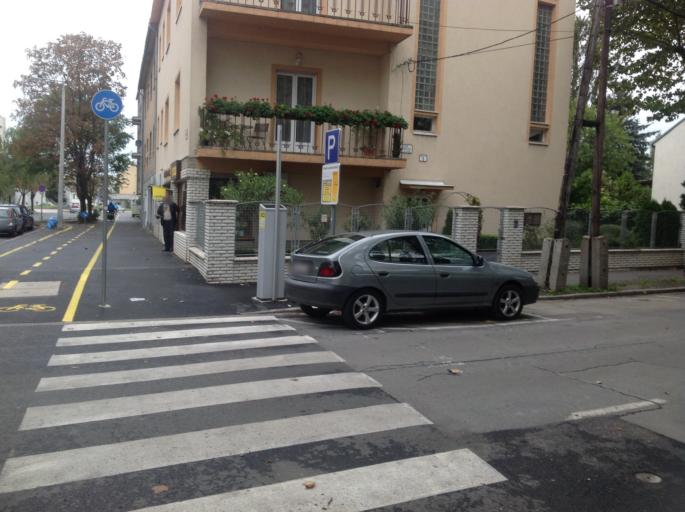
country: HU
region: Gyor-Moson-Sopron
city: Gyor
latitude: 47.6928
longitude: 17.6308
